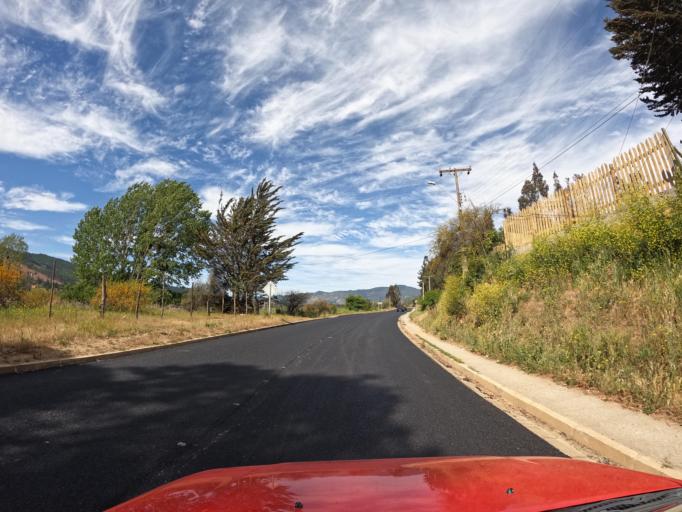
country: CL
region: Maule
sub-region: Provincia de Talca
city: Constitucion
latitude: -35.0976
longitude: -72.0071
